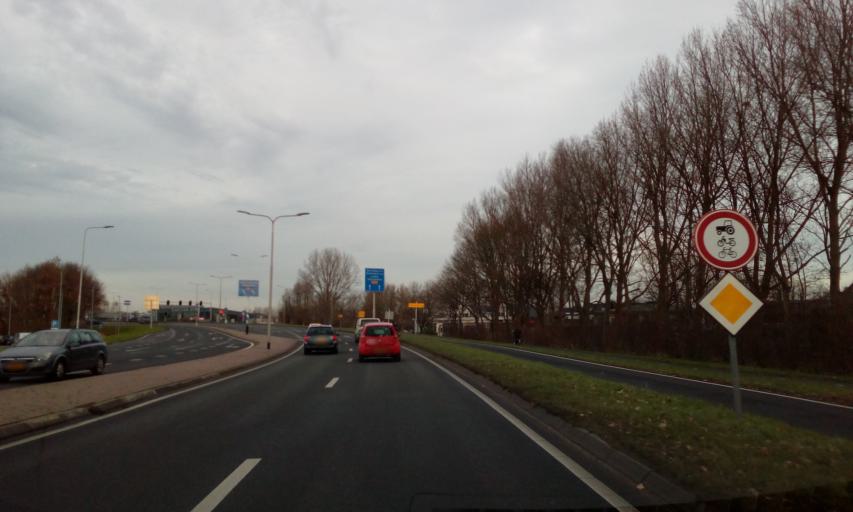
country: NL
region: South Holland
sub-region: Gemeente Leiden
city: Leiden
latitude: 52.1271
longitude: 4.4955
